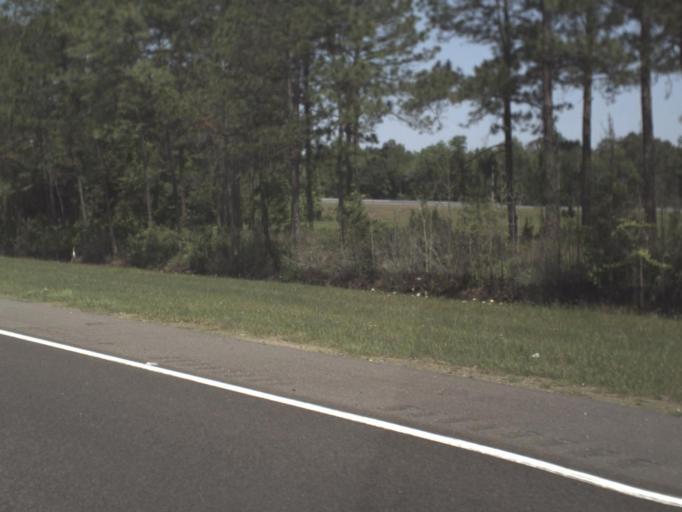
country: US
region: Florida
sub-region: Duval County
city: Baldwin
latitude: 30.3066
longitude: -81.8802
